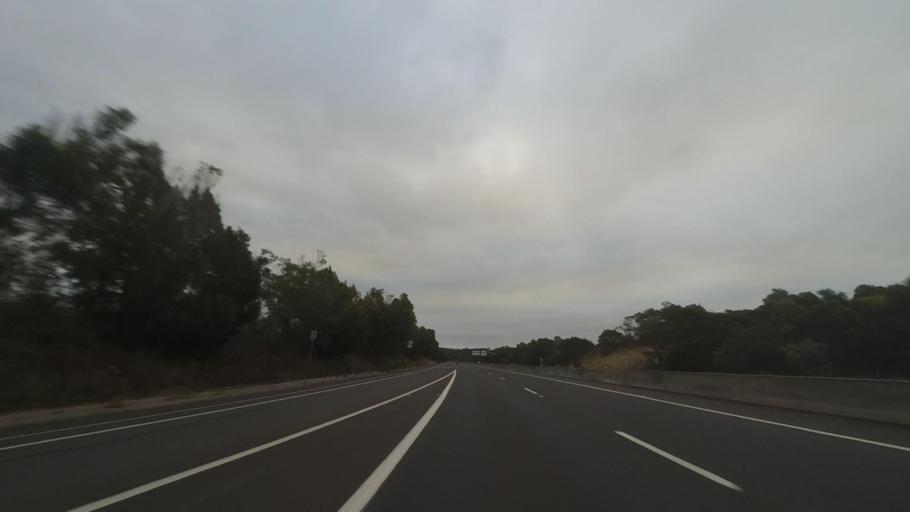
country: AU
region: New South Wales
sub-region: Kiama
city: Kiama
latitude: -34.6496
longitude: 150.8468
